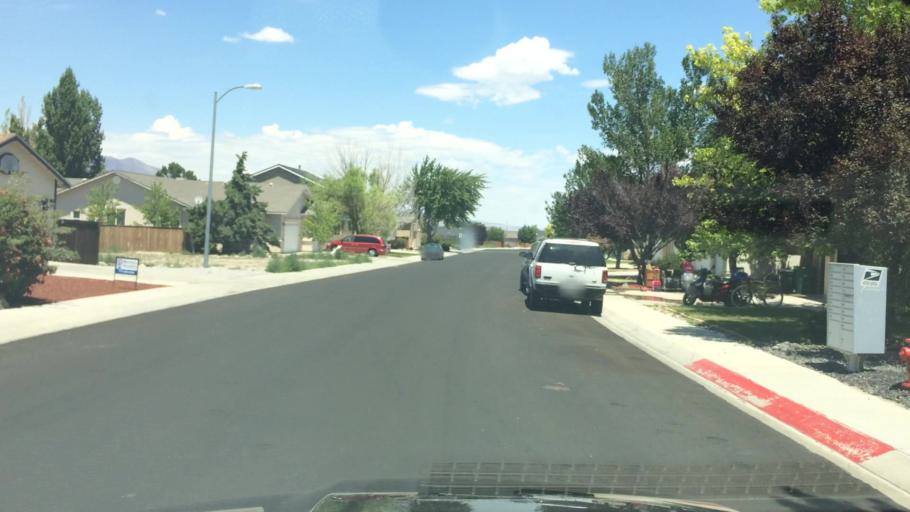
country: US
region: Nevada
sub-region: Lyon County
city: Fernley
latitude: 39.5872
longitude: -119.1410
